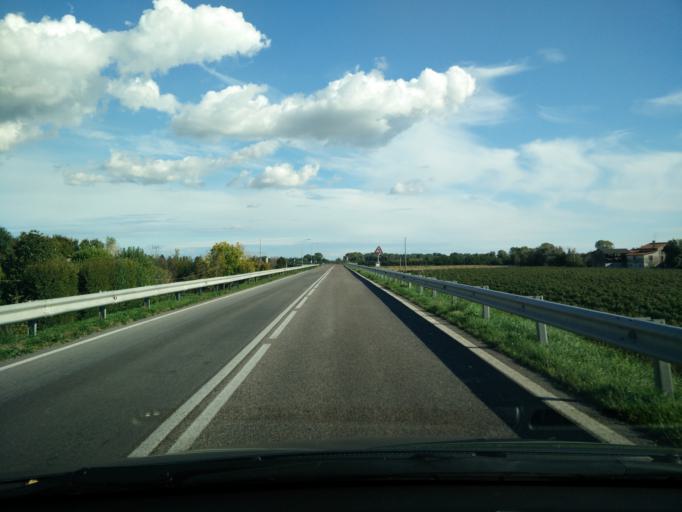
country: IT
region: Veneto
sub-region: Provincia di Treviso
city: Talponada
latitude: 45.6950
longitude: 12.4854
